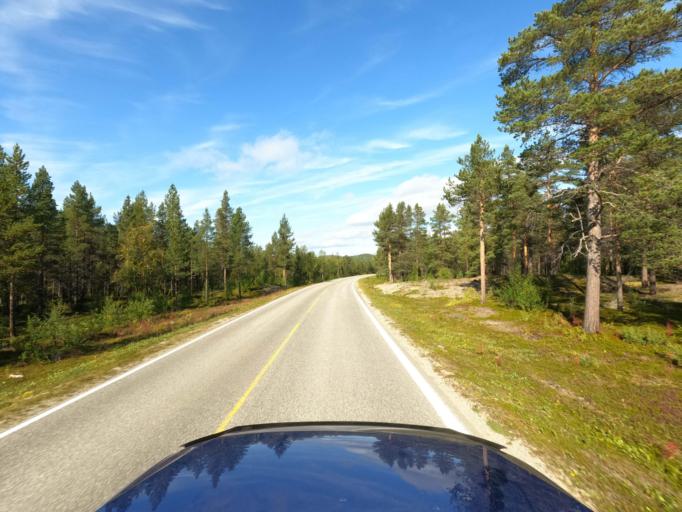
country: NO
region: Finnmark Fylke
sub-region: Porsanger
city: Lakselv
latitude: 69.8166
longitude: 25.1577
